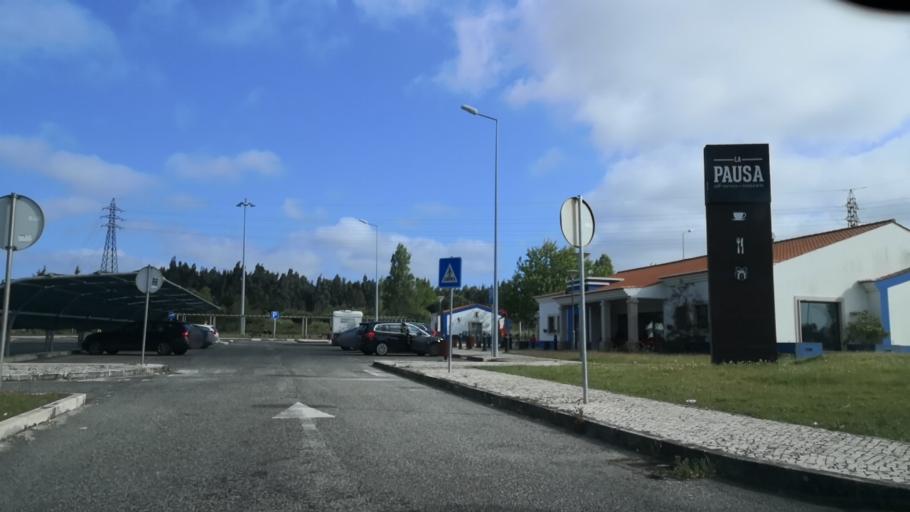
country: PT
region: Leiria
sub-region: Caldas da Rainha
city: Caldas da Rainha
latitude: 39.3865
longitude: -9.1501
